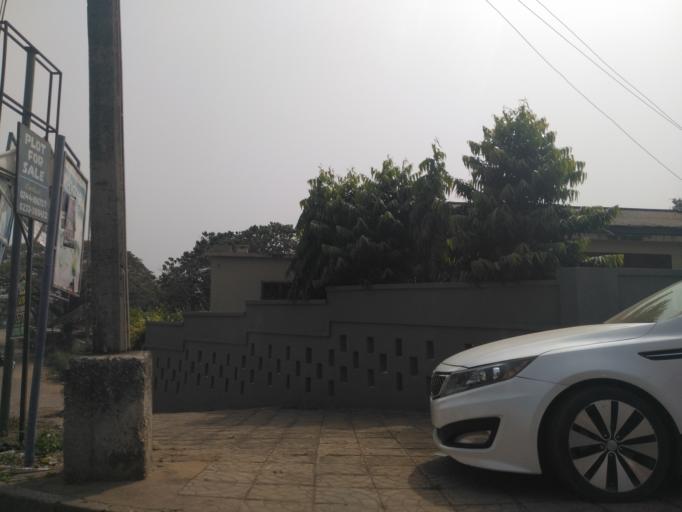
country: GH
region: Ashanti
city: Kumasi
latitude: 6.6830
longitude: -1.6031
